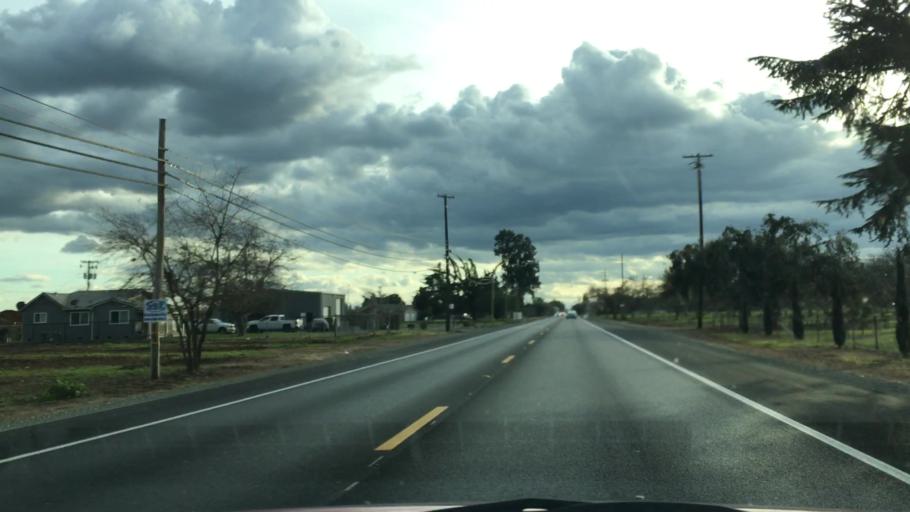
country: US
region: California
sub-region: San Joaquin County
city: Morada
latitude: 38.0115
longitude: -121.2127
